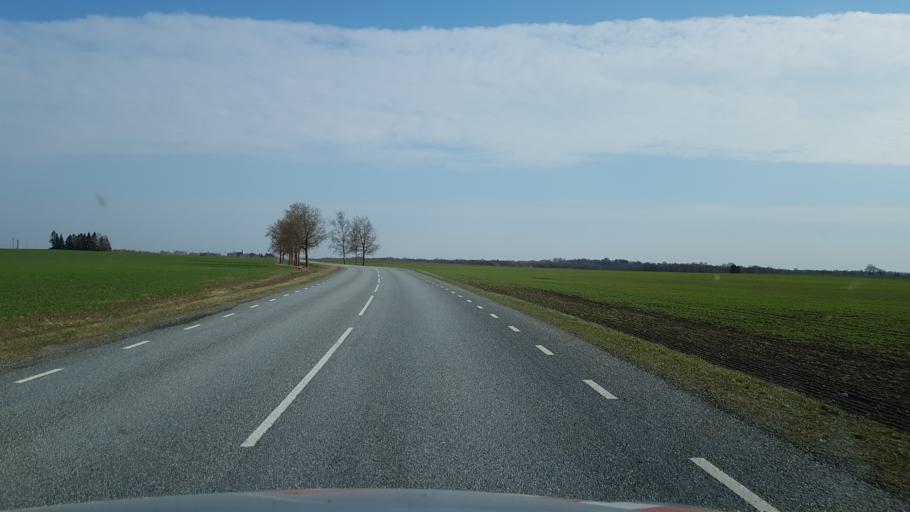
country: EE
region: Laeaene-Virumaa
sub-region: Kadrina vald
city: Kadrina
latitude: 59.3626
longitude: 26.1088
